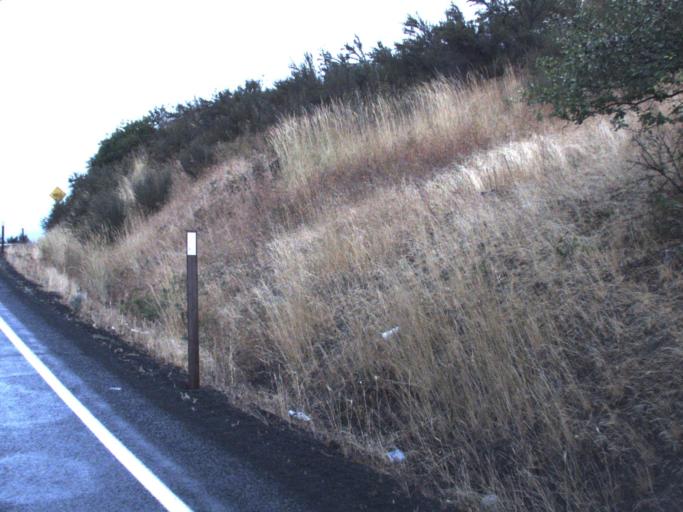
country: US
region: Washington
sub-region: Lincoln County
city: Davenport
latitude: 47.7725
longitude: -117.8936
